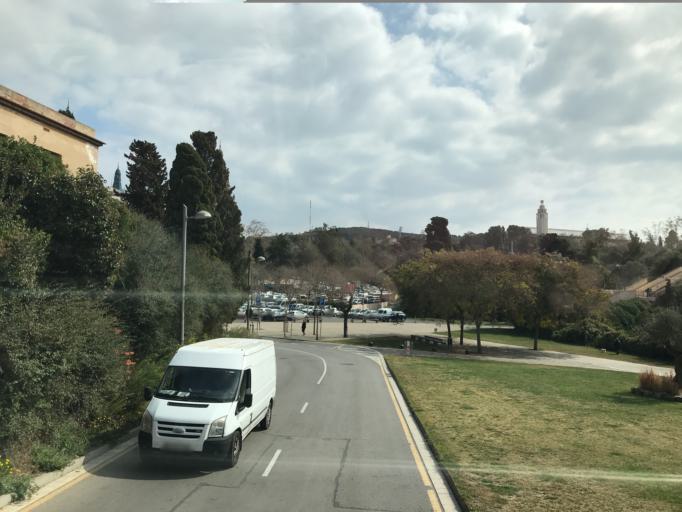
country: ES
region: Catalonia
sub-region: Provincia de Barcelona
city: Sants-Montjuic
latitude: 41.3682
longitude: 2.1503
